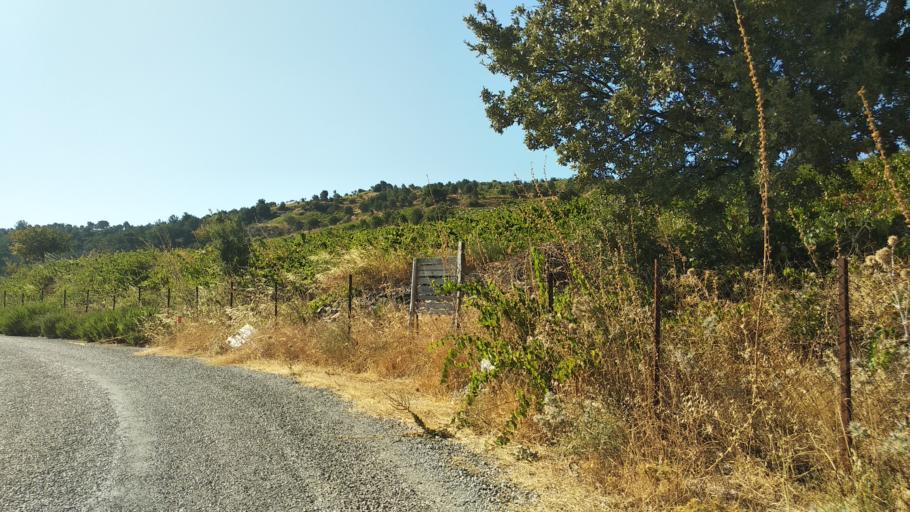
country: TR
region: Izmir
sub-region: Seferihisar
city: Seferhisar
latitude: 38.3292
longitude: 26.9482
